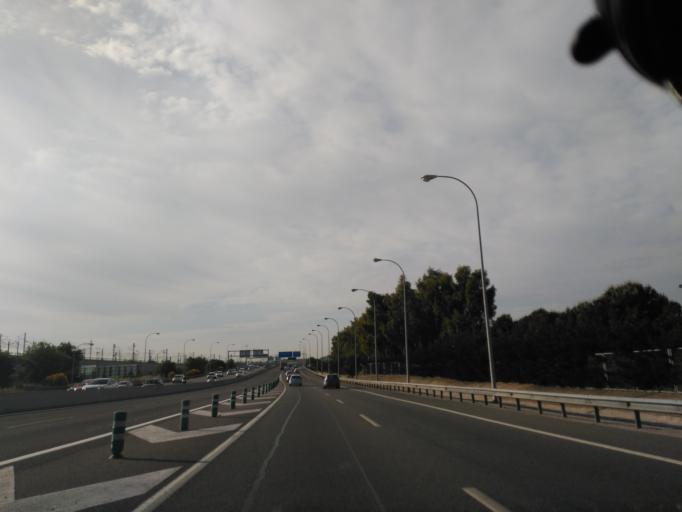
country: ES
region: Madrid
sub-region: Provincia de Madrid
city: Usera
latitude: 40.3771
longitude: -3.6845
